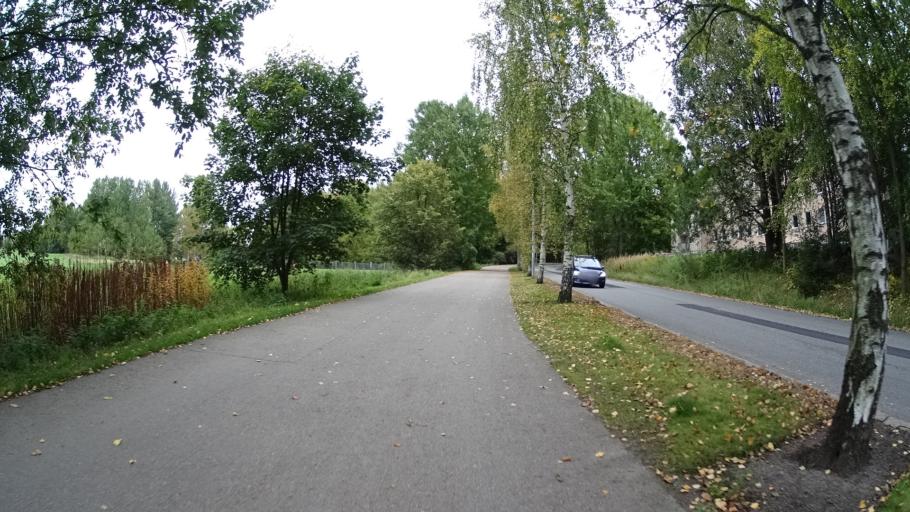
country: FI
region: Uusimaa
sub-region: Helsinki
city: Teekkarikylae
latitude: 60.2086
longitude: 24.8620
